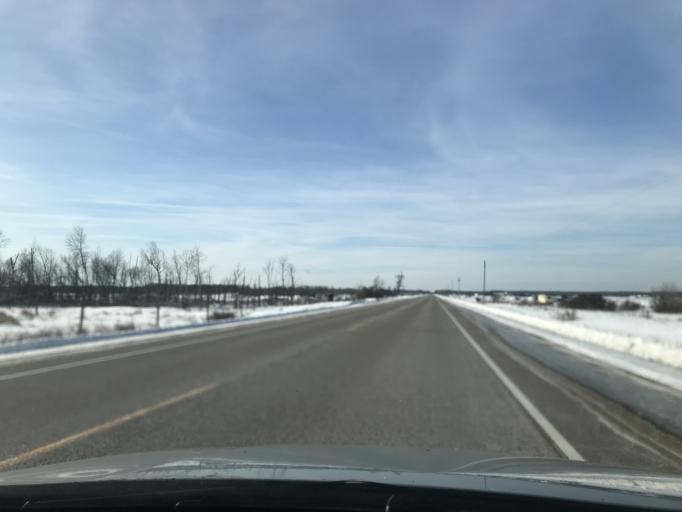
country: US
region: Wisconsin
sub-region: Oconto County
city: Gillett
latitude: 45.1136
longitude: -88.2940
